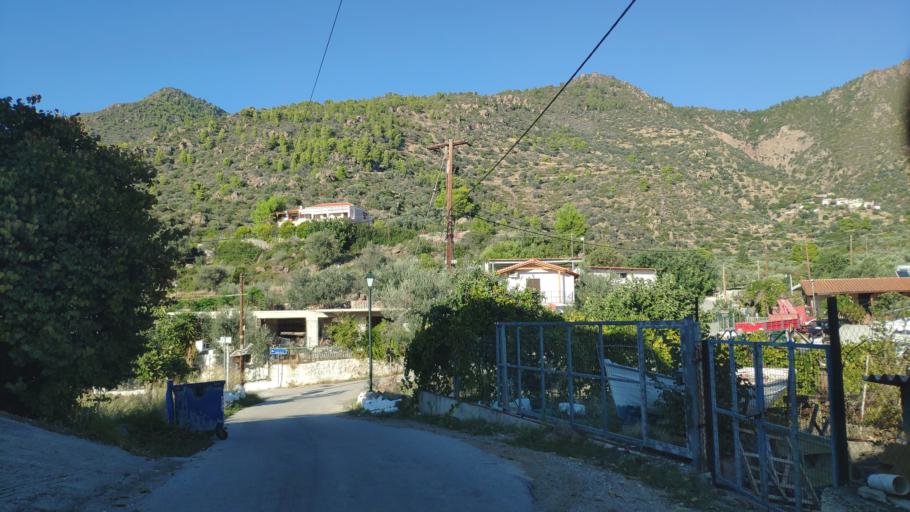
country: GR
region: Attica
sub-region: Nomos Piraios
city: Megalochori
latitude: 37.5926
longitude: 23.3408
